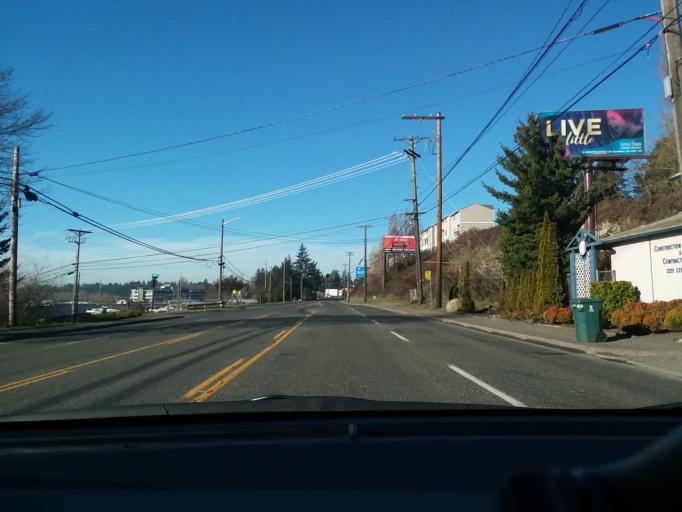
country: US
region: Washington
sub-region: Pierce County
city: Fircrest
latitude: 47.2331
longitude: -122.4784
